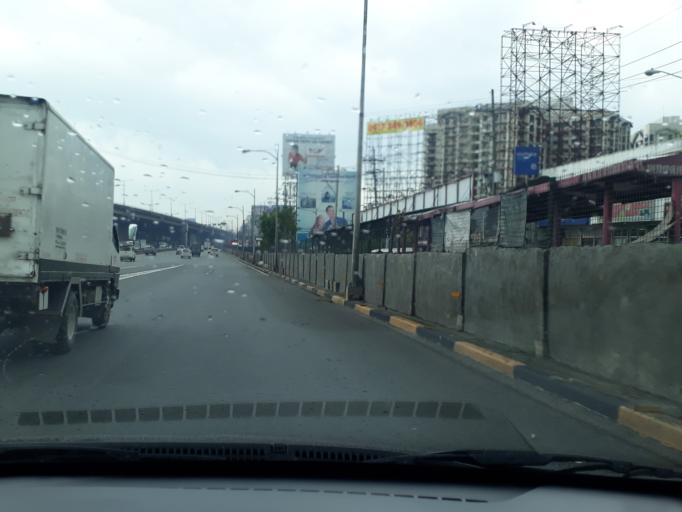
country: PH
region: Metro Manila
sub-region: Makati City
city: Makati City
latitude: 14.5089
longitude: 121.0336
